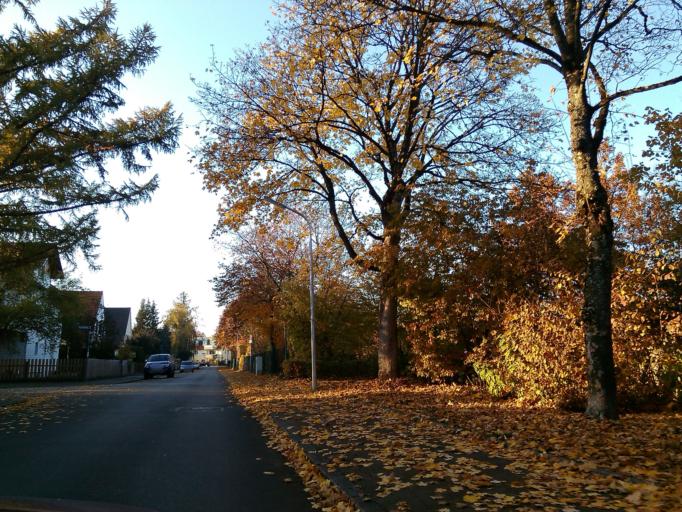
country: DE
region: Bavaria
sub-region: Upper Bavaria
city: Pasing
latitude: 48.1417
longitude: 11.4455
